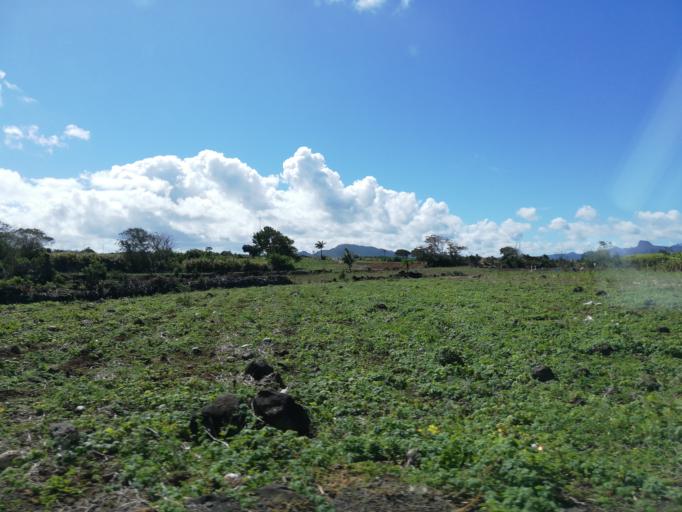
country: MU
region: Grand Port
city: Beau Vallon
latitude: -20.4448
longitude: 57.6926
